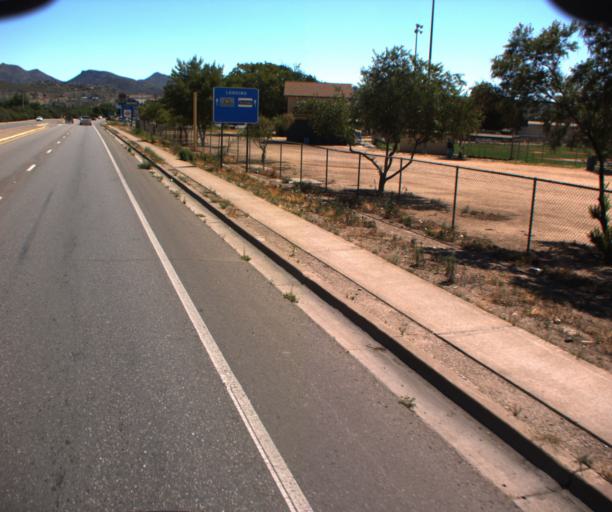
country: US
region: Arizona
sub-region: Gila County
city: Claypool
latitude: 33.4125
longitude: -110.8402
